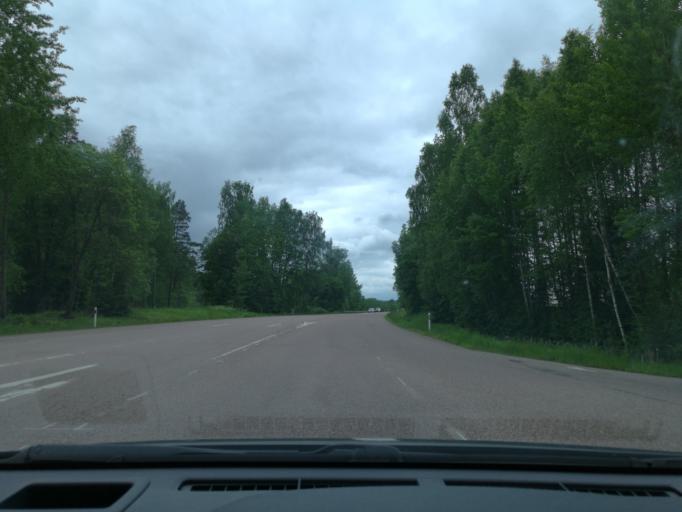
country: SE
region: Dalarna
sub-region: Smedjebackens Kommun
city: Smedjebacken
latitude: 60.1407
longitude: 15.3429
